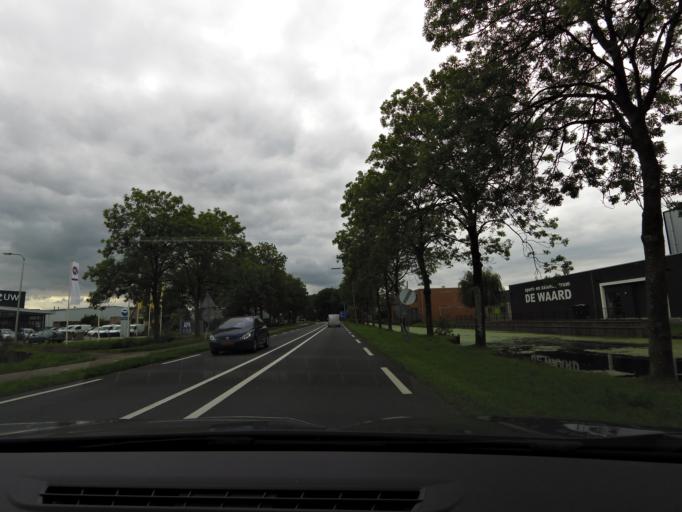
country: NL
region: South Holland
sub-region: Molenwaard
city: Liesveld
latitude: 51.9330
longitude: 4.7910
